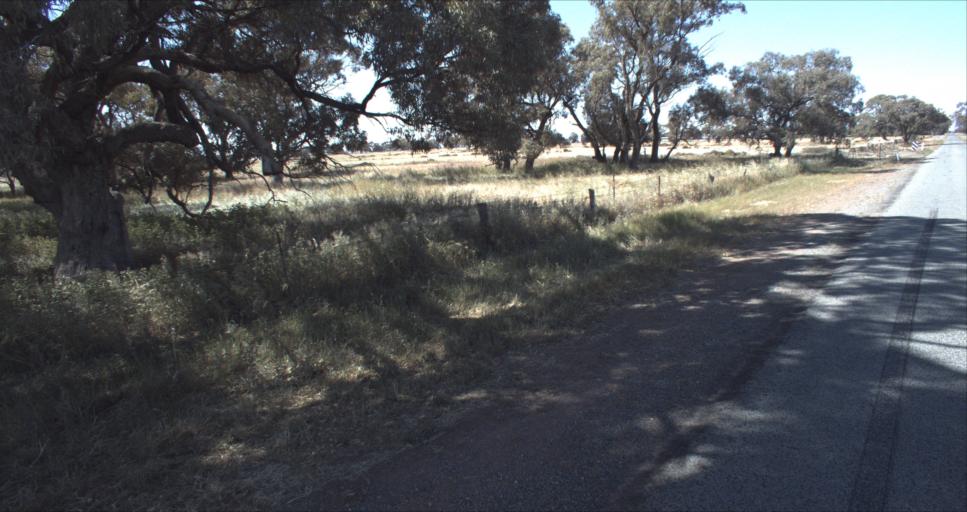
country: AU
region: New South Wales
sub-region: Leeton
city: Leeton
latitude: -34.5389
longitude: 146.3169
